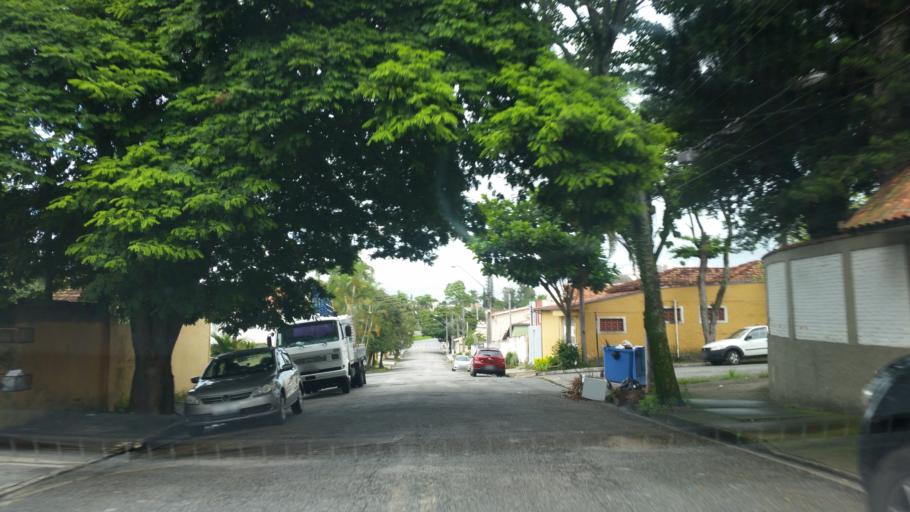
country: BR
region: Sao Paulo
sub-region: Taubate
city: Taubate
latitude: -23.0339
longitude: -45.5690
